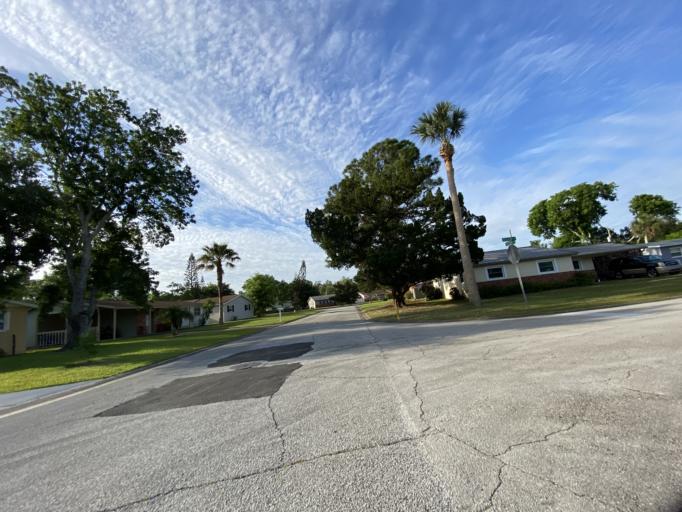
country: US
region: Florida
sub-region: Volusia County
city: South Daytona
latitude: 29.1752
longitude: -81.0112
